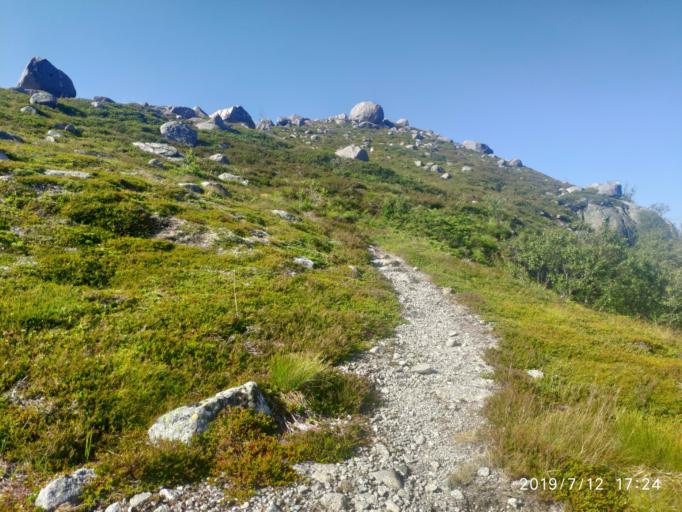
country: NO
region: Rogaland
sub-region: Forsand
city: Forsand
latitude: 58.9942
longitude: 6.1708
